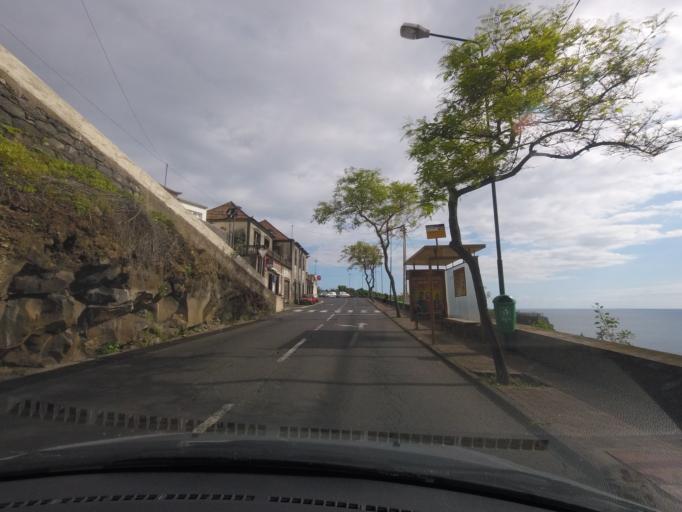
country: PT
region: Madeira
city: Camara de Lobos
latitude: 32.6449
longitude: -16.9652
